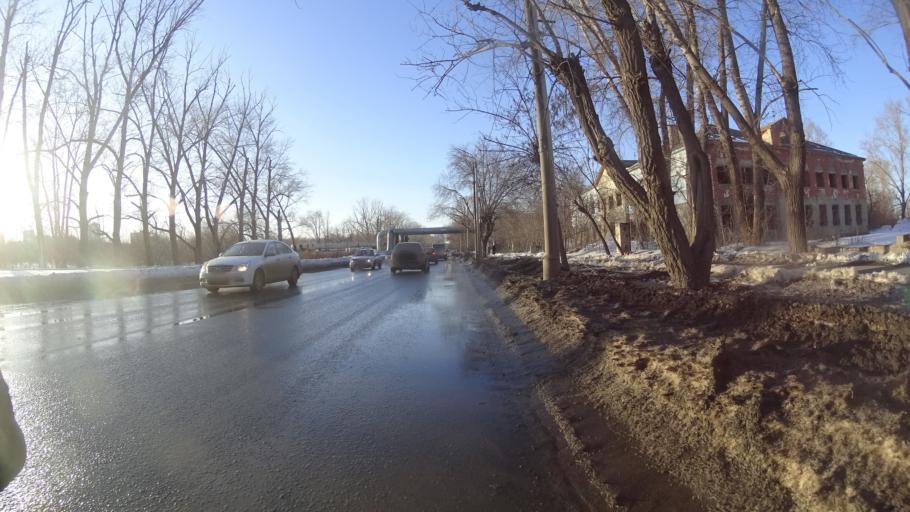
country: RU
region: Chelyabinsk
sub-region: Gorod Chelyabinsk
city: Chelyabinsk
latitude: 55.1316
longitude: 61.4631
